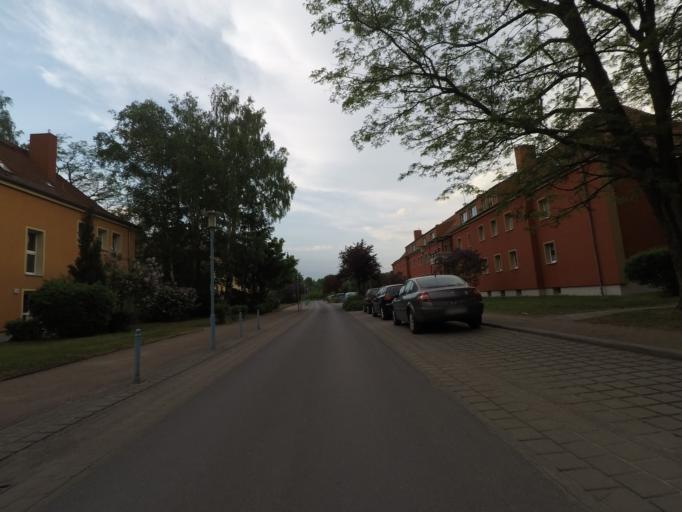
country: DE
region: Brandenburg
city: Eberswalde
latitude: 52.8450
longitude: 13.7452
